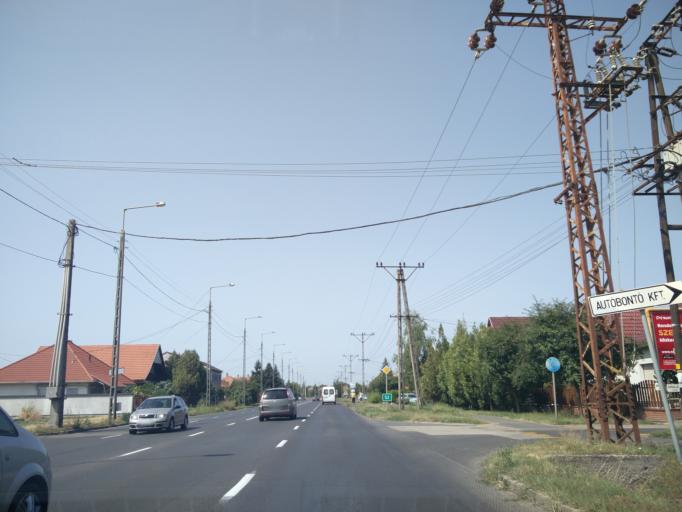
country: HU
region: Csongrad
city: Szeged
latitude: 46.2719
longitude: 20.0846
